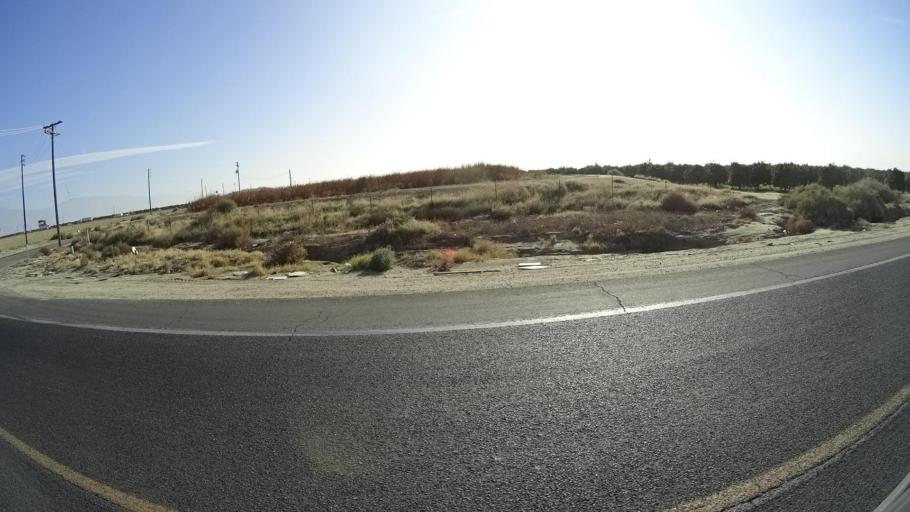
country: US
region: California
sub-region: Kern County
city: Lamont
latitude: 35.3369
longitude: -118.8256
